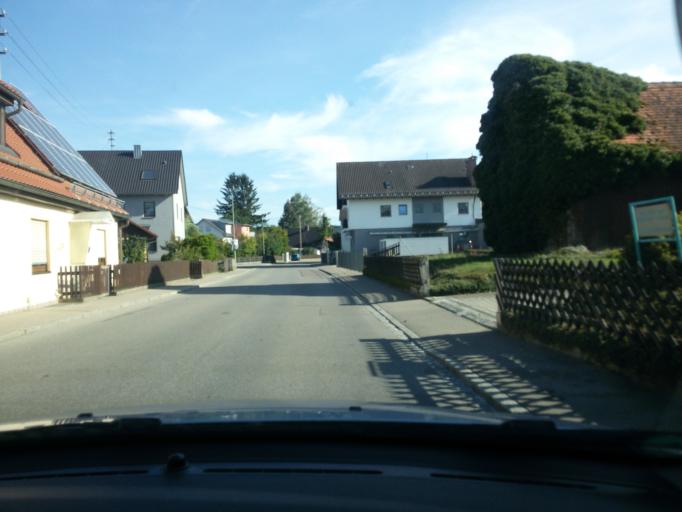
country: DE
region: Bavaria
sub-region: Swabia
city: Gessertshausen
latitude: 48.3420
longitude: 10.7338
